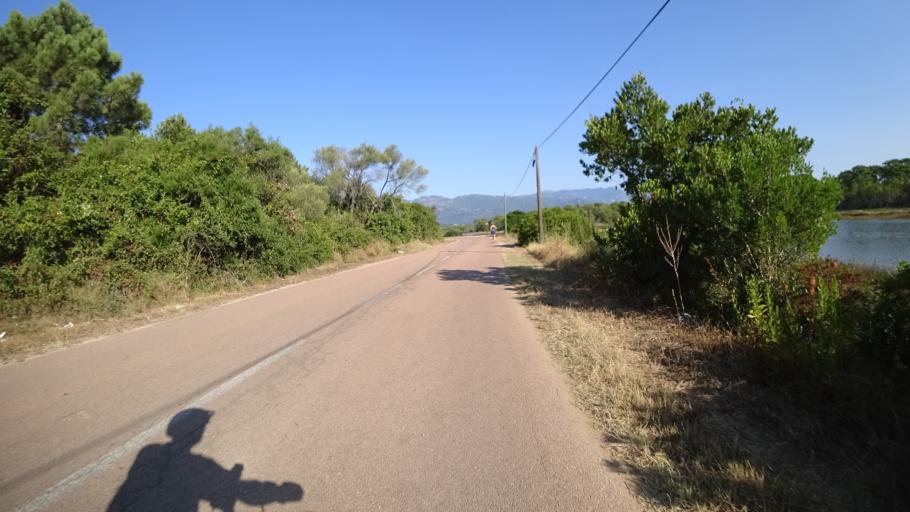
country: FR
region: Corsica
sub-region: Departement de la Corse-du-Sud
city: Porto-Vecchio
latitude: 41.6180
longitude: 9.3263
